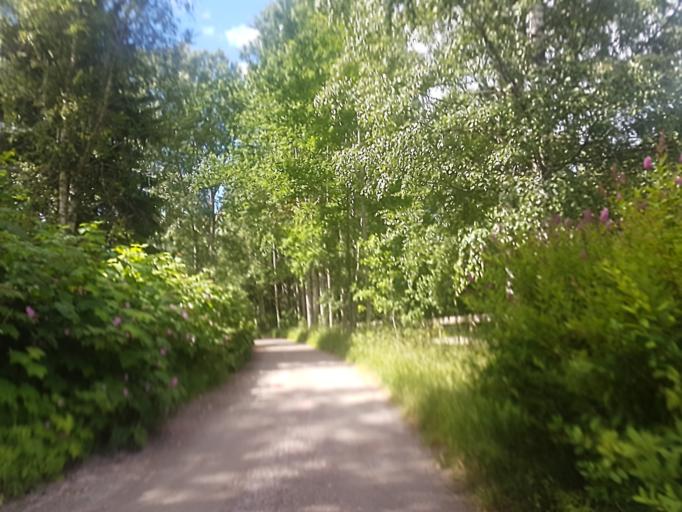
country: SE
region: Soedermanland
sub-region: Gnesta Kommun
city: Gnesta
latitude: 59.0340
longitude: 17.3493
